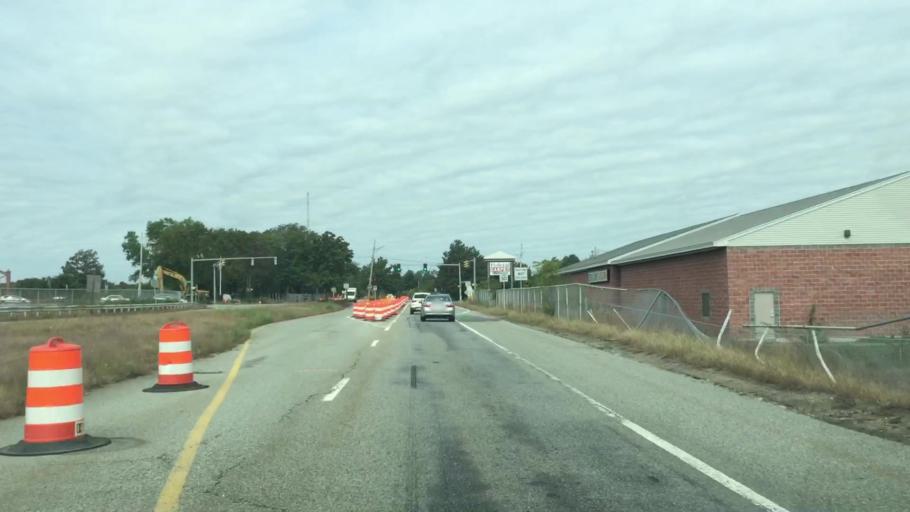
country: US
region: Massachusetts
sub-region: Middlesex County
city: Dracut
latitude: 42.6549
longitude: -71.3129
